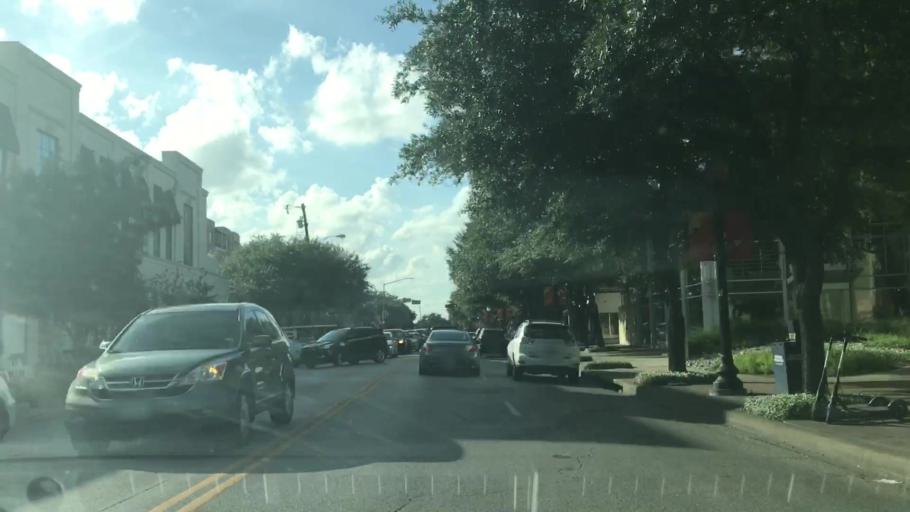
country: US
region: Texas
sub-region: Dallas County
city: Highland Park
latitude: 32.8226
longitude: -96.7873
